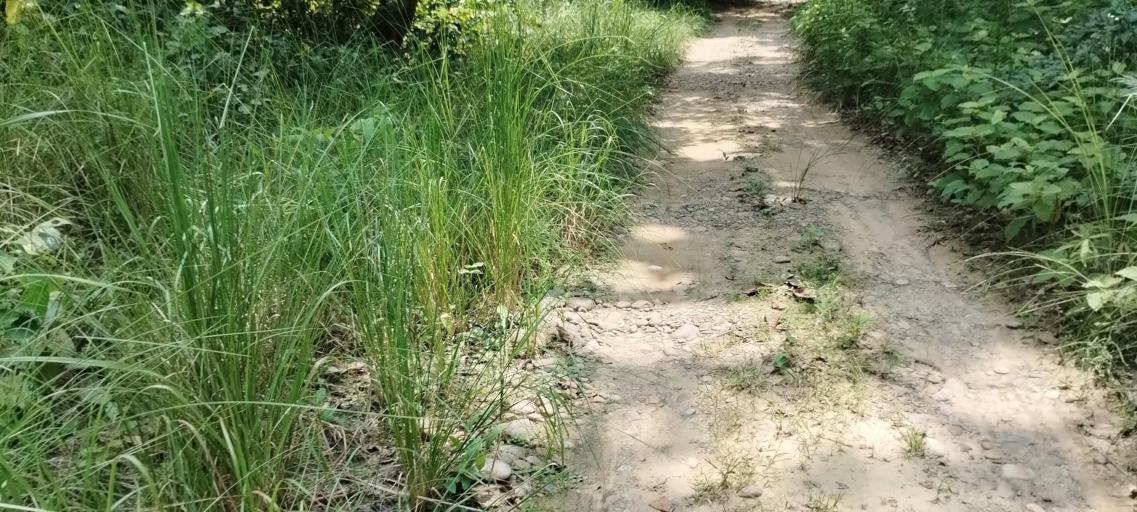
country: NP
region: Far Western
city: Tikapur
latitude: 28.4990
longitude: 81.2560
